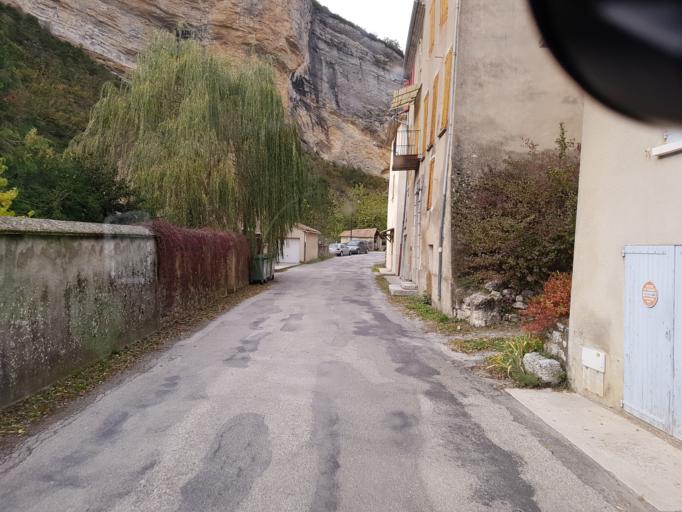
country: FR
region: Provence-Alpes-Cote d'Azur
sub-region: Departement des Hautes-Alpes
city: Serres
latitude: 44.3128
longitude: 5.6909
